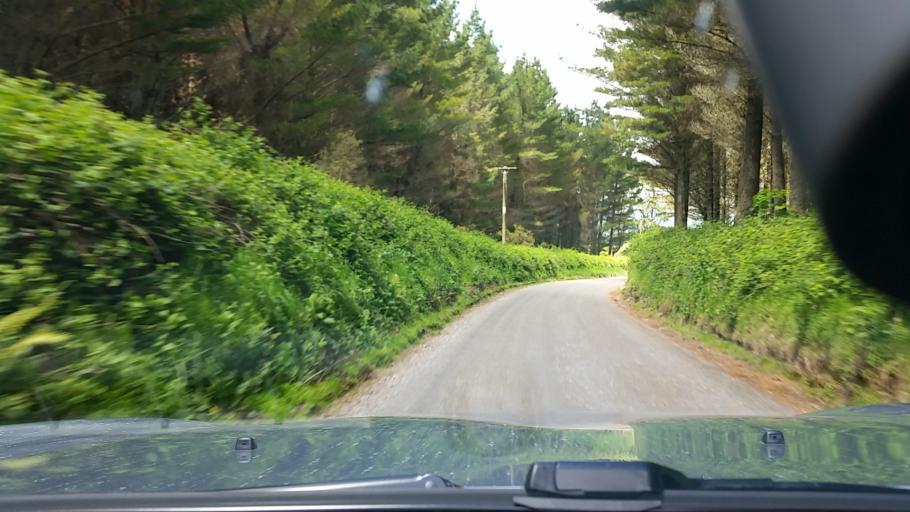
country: NZ
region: Bay of Plenty
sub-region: Rotorua District
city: Rotorua
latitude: -38.2215
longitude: 176.1609
